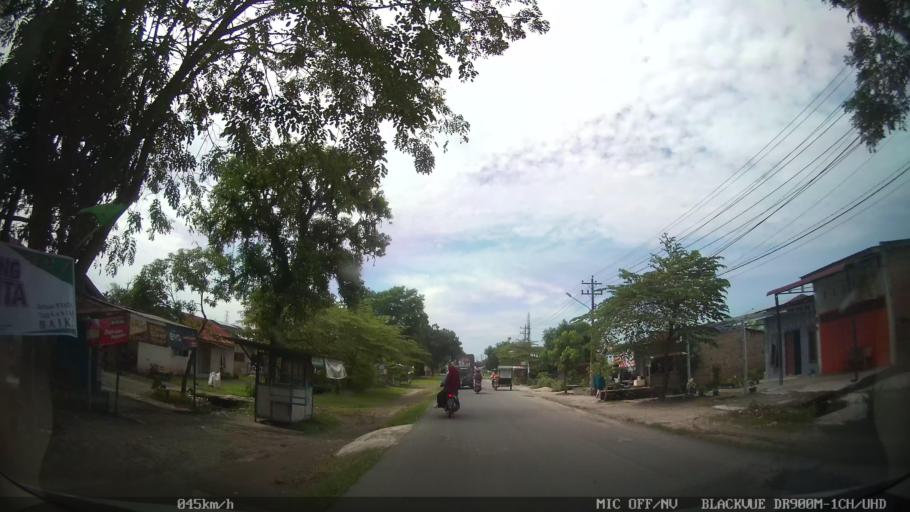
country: ID
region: North Sumatra
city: Percut
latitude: 3.6037
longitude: 98.8075
